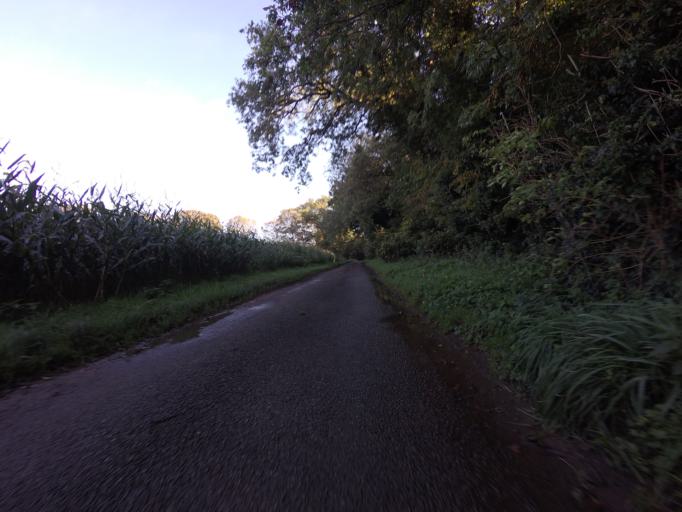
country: GB
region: England
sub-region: Norfolk
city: Dersingham
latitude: 52.8338
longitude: 0.5716
